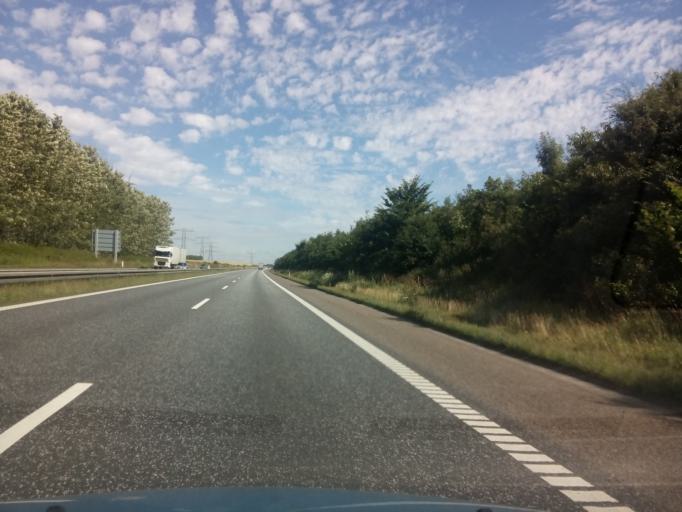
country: DK
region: Central Jutland
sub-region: Arhus Kommune
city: Trige
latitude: 56.2560
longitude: 10.1256
